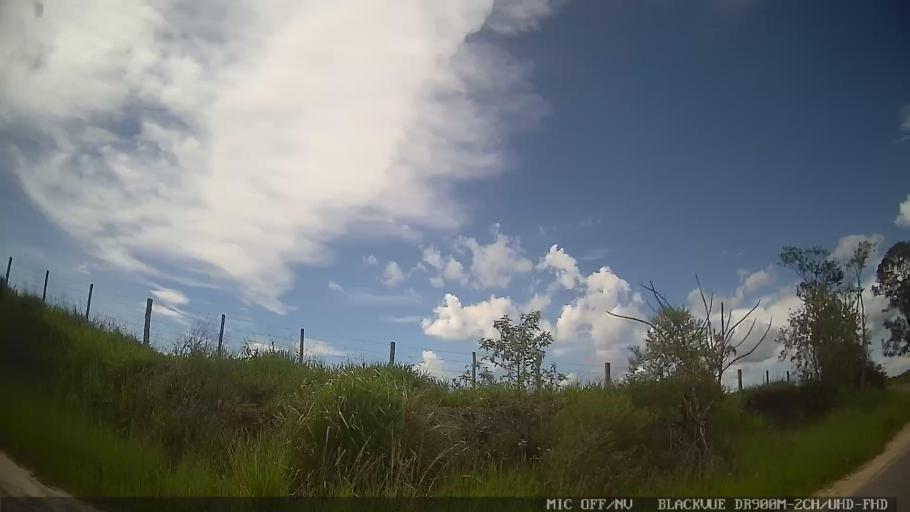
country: BR
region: Sao Paulo
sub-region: Conchas
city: Conchas
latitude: -22.9500
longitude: -47.9829
